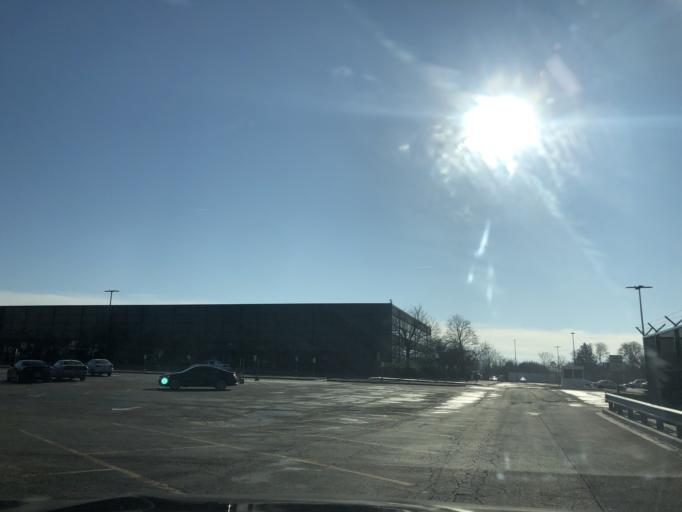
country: US
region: Illinois
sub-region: Cook County
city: Forest Park
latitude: 41.8740
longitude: -87.8275
